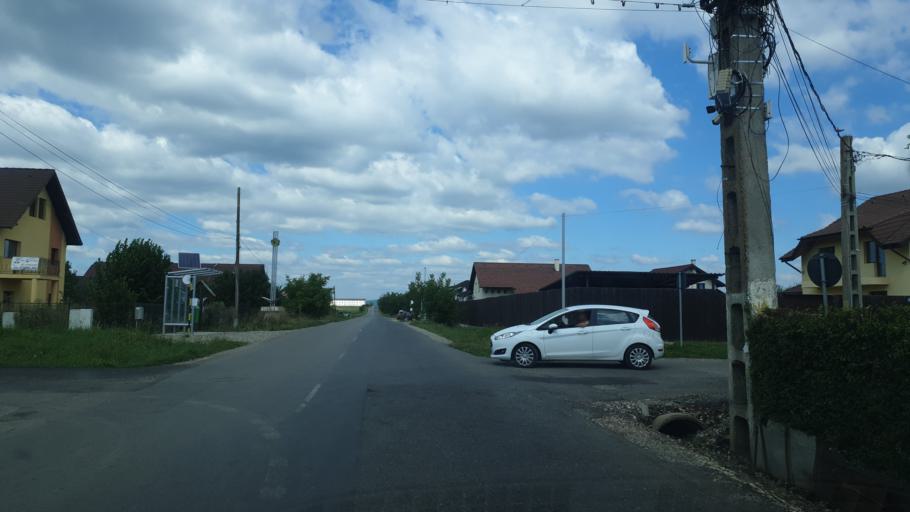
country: RO
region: Brasov
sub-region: Comuna Sanpetru
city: Sanpetru
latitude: 45.7193
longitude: 25.6276
